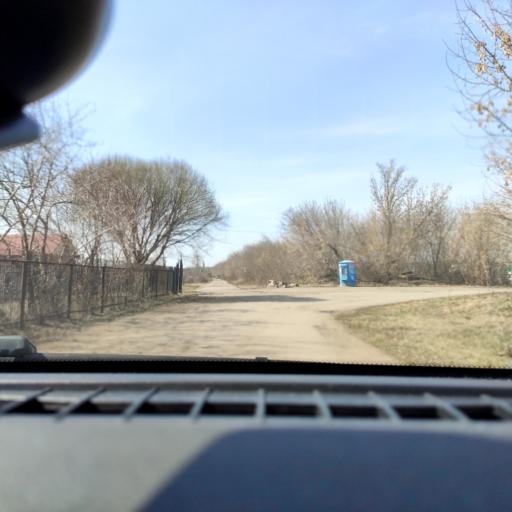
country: RU
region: Samara
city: Podstepki
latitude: 53.5211
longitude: 49.0985
